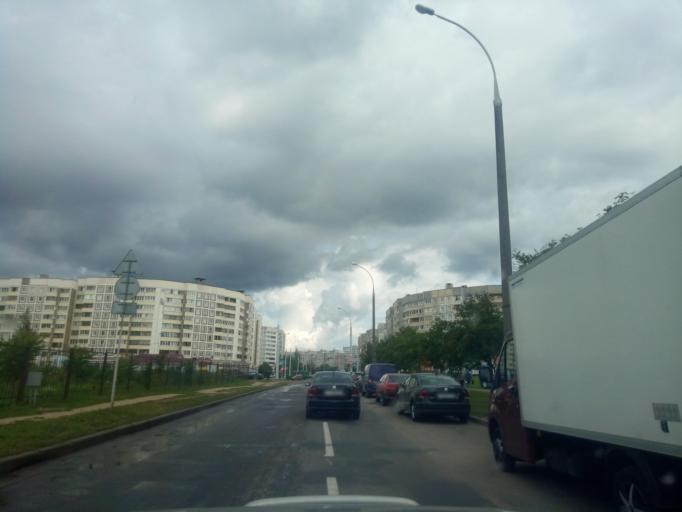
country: BY
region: Minsk
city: Novoye Medvezhino
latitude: 53.8811
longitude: 27.4399
